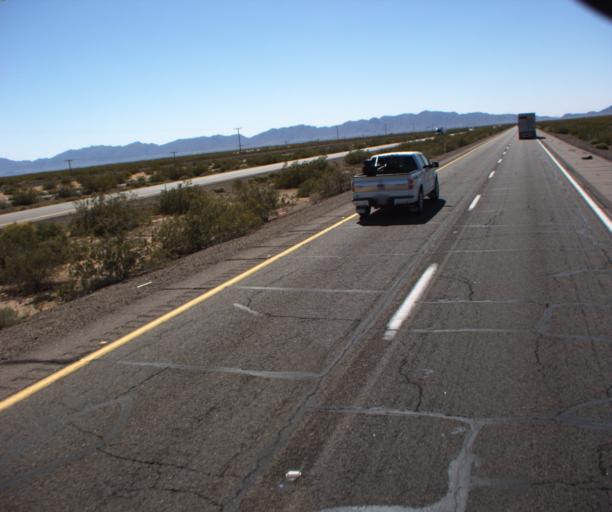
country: US
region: Arizona
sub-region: Yuma County
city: Wellton
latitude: 32.7852
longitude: -113.5716
